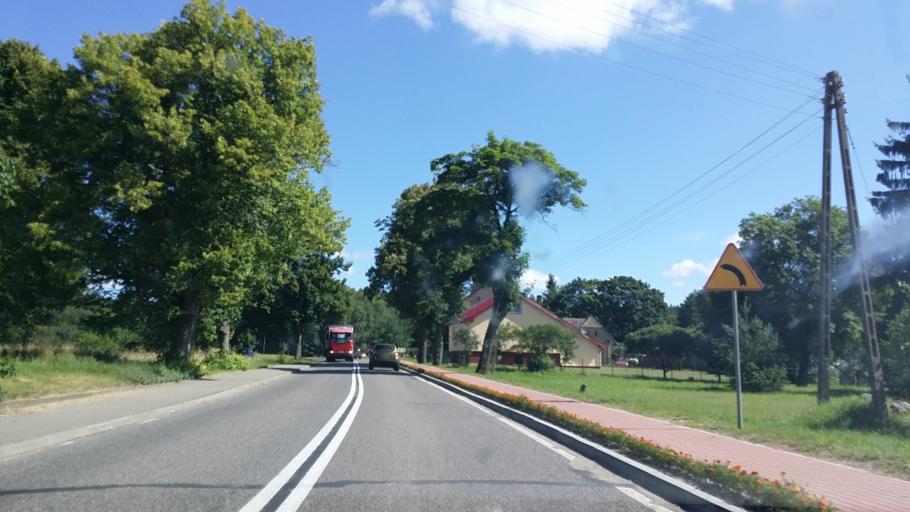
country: PL
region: West Pomeranian Voivodeship
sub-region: Powiat drawski
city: Drawsko Pomorskie
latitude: 53.4434
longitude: 15.8295
